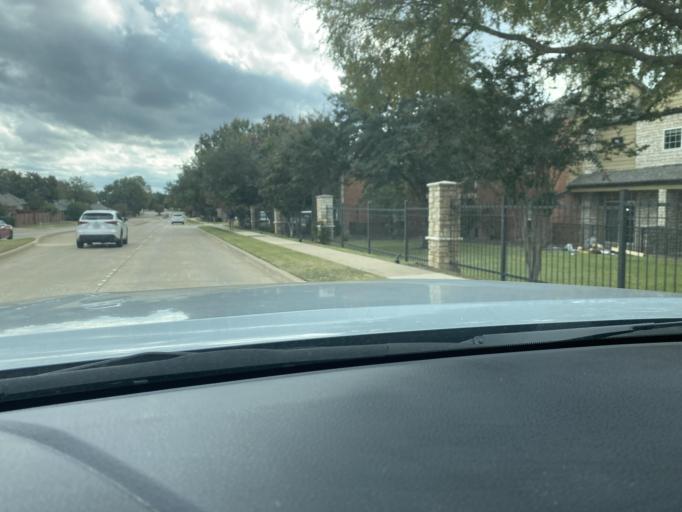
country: US
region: Texas
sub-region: Dallas County
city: Addison
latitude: 33.0349
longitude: -96.7900
